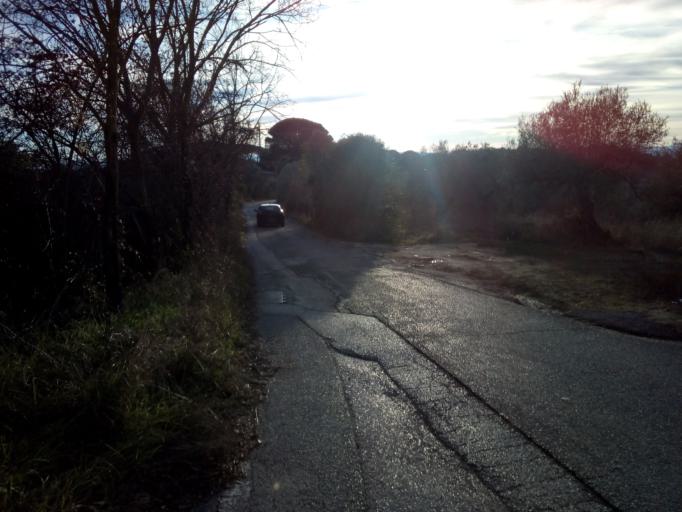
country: IT
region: Umbria
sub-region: Provincia di Perugia
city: Perugia
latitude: 43.0947
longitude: 12.3949
